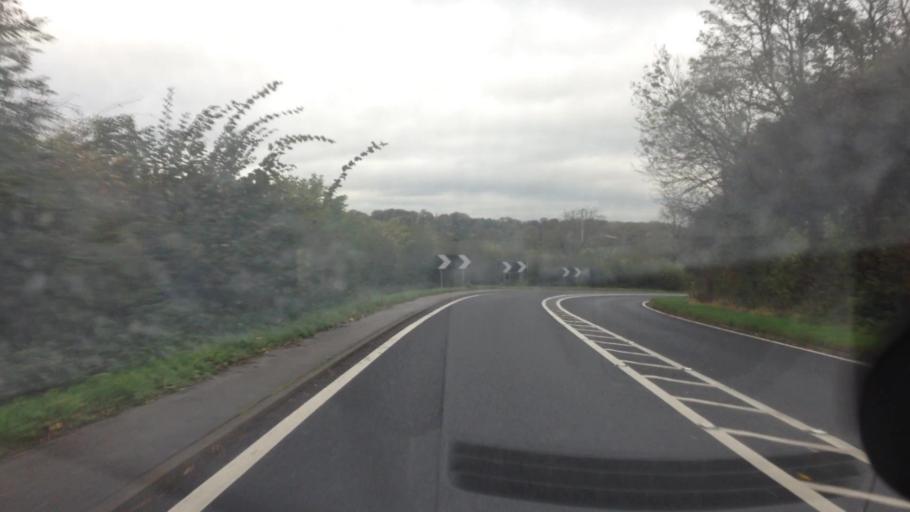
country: GB
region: England
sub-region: City and Borough of Leeds
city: Shadwell
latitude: 53.8553
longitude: -1.4619
